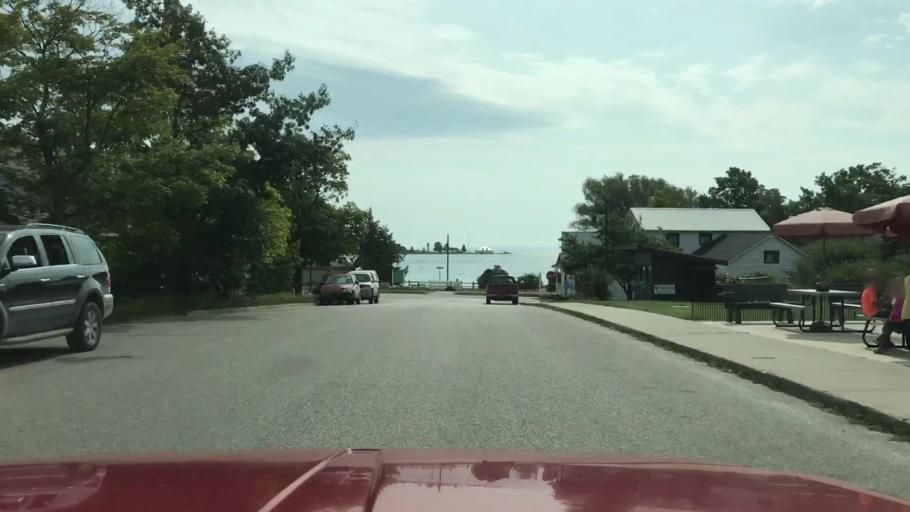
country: US
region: Michigan
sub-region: Charlevoix County
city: Charlevoix
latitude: 45.7465
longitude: -85.5216
